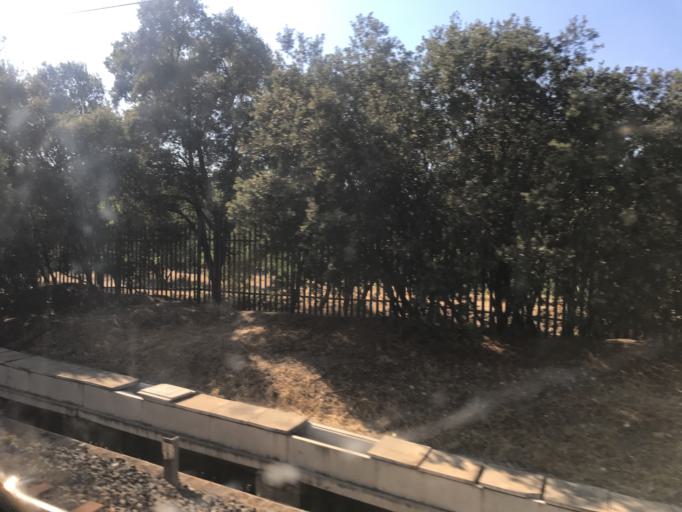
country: ES
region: Madrid
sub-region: Provincia de Madrid
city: Moncloa-Aravaca
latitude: 40.4161
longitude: -3.7421
